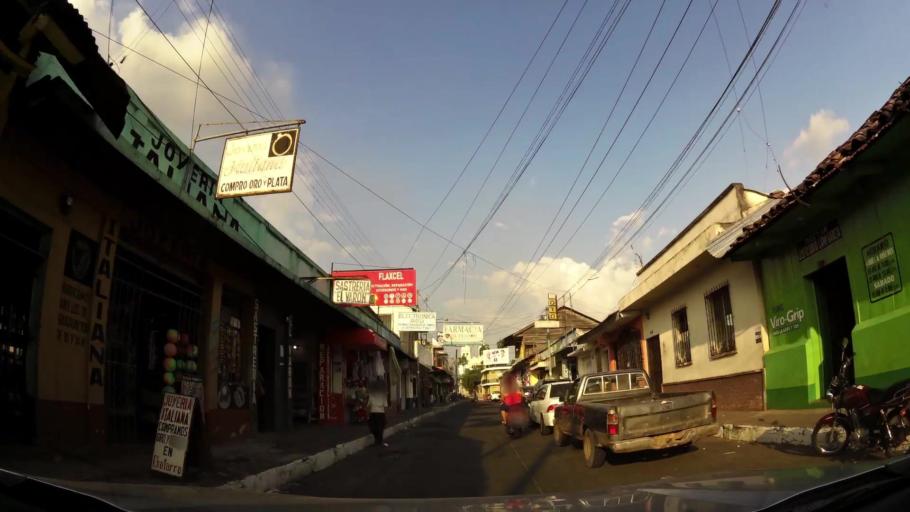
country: GT
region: Retalhuleu
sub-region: Municipio de Retalhuleu
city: Retalhuleu
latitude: 14.5349
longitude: -91.6800
